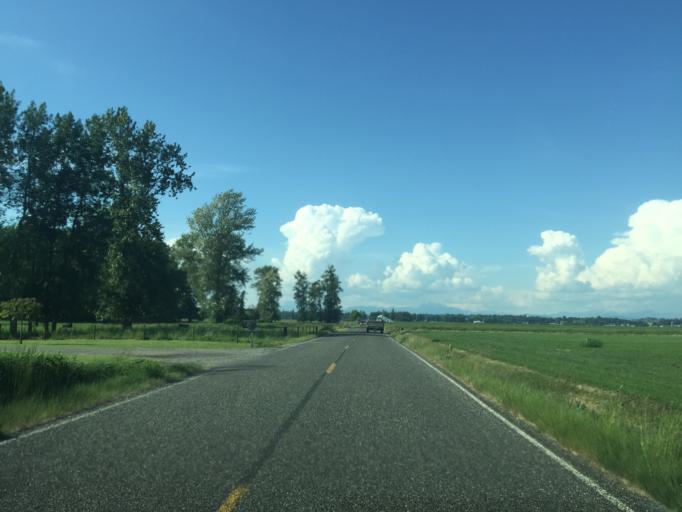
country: US
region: Washington
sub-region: Whatcom County
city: Lynden
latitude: 48.9814
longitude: -122.4406
